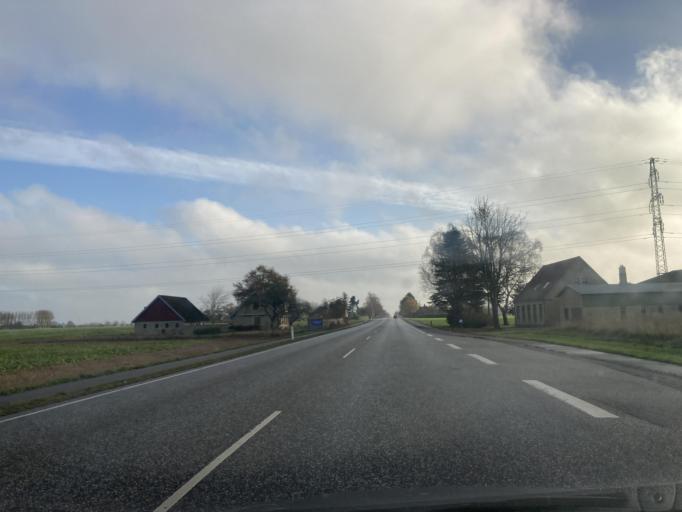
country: DK
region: Zealand
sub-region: Guldborgsund Kommune
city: Sakskobing
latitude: 54.7860
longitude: 11.6913
